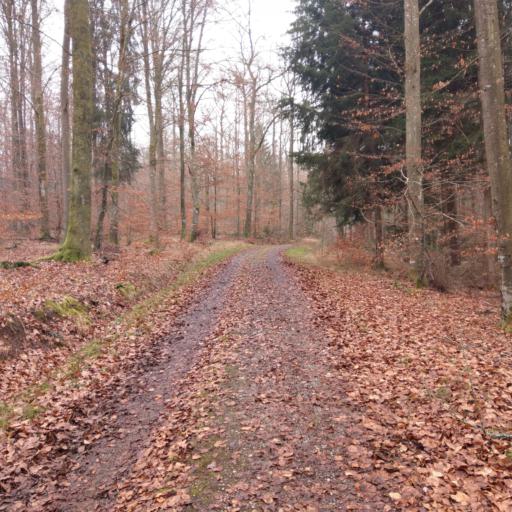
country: DE
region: Baden-Wuerttemberg
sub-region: Tuebingen Region
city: Dettenhausen
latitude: 48.6277
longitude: 9.1085
